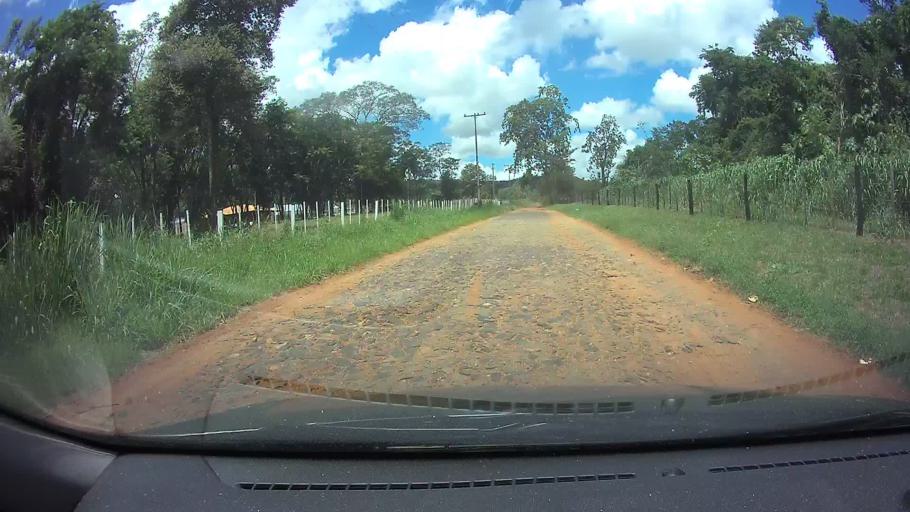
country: PY
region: Paraguari
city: La Colmena
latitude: -25.9196
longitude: -56.7942
